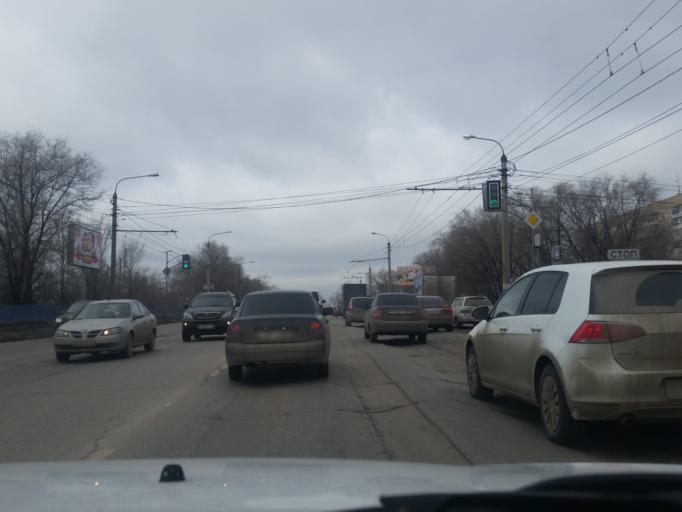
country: RU
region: Ulyanovsk
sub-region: Ulyanovskiy Rayon
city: Ulyanovsk
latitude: 54.3372
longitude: 48.5428
